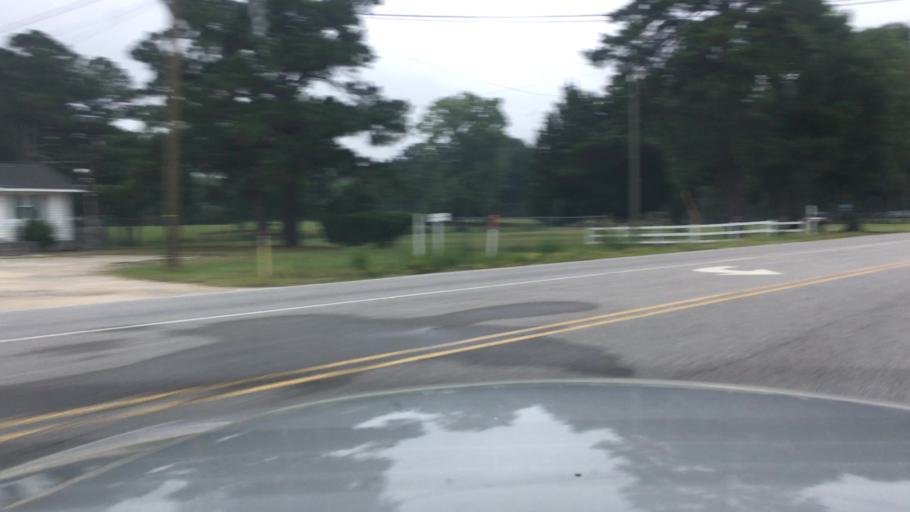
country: US
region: North Carolina
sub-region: Cumberland County
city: Fayetteville
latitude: 35.0103
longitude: -78.8638
